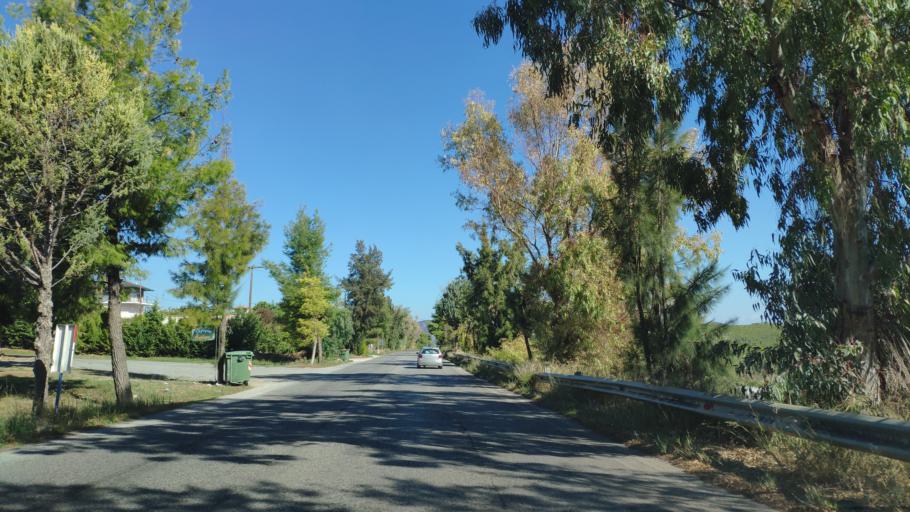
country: GR
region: Peloponnese
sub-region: Nomos Korinthias
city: Khiliomodhi
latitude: 37.8155
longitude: 22.8725
